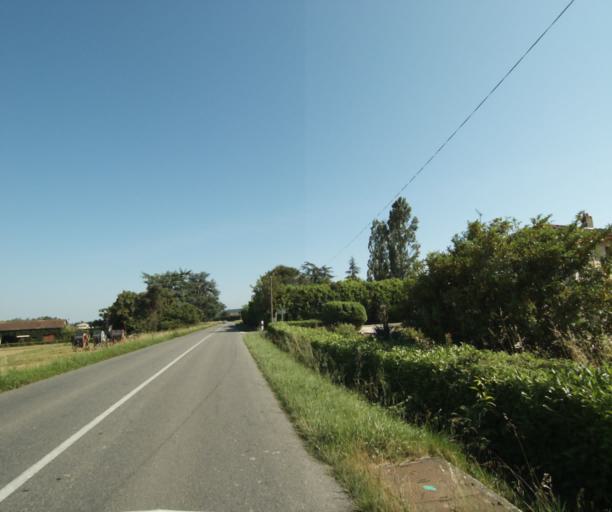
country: FR
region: Midi-Pyrenees
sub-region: Departement du Tarn-et-Garonne
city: Corbarieu
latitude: 43.9585
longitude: 1.3625
